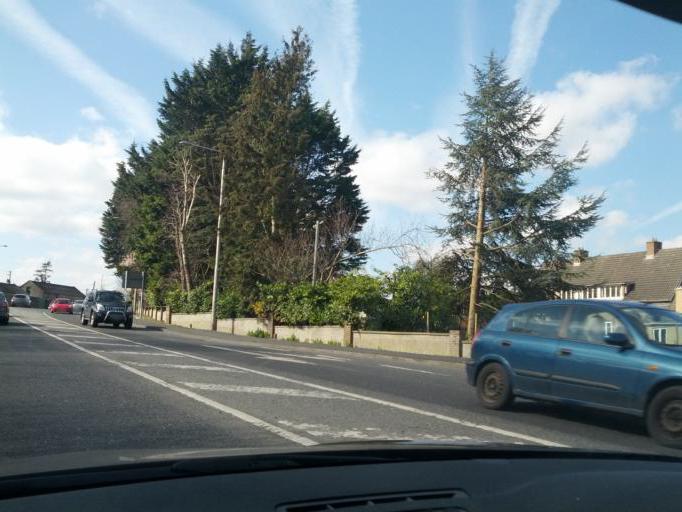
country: IE
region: Leinster
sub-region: Kildare
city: Leixlip
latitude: 53.3668
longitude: -6.4949
